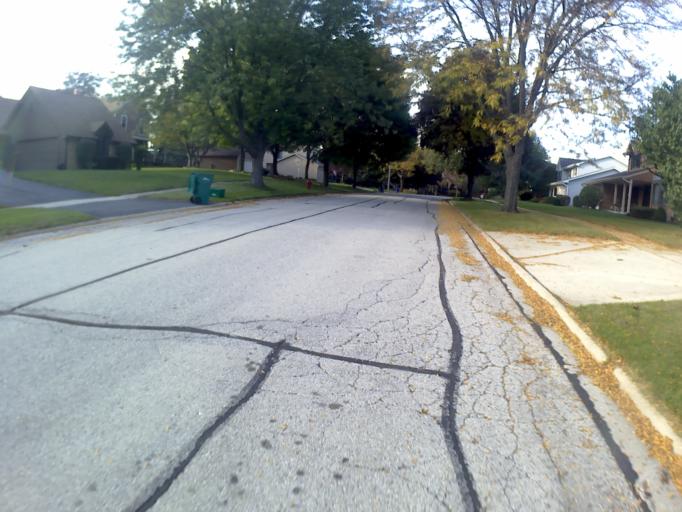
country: US
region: Illinois
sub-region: DuPage County
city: Lisle
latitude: 41.7731
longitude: -88.0692
